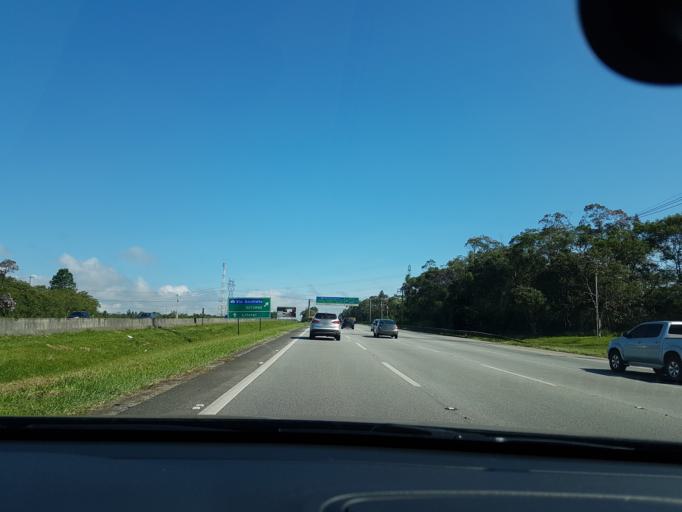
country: BR
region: Sao Paulo
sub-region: Cubatao
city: Cubatao
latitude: -23.8850
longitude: -46.5670
